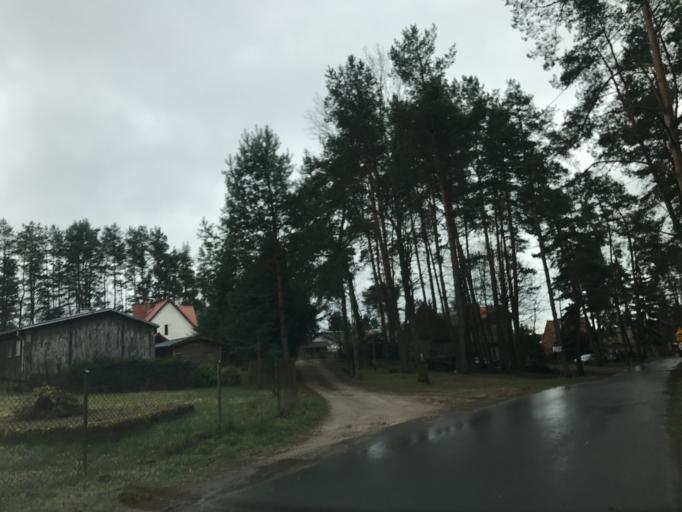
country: PL
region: Warmian-Masurian Voivodeship
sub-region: Powiat olsztynski
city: Stawiguda
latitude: 53.7135
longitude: 20.3778
